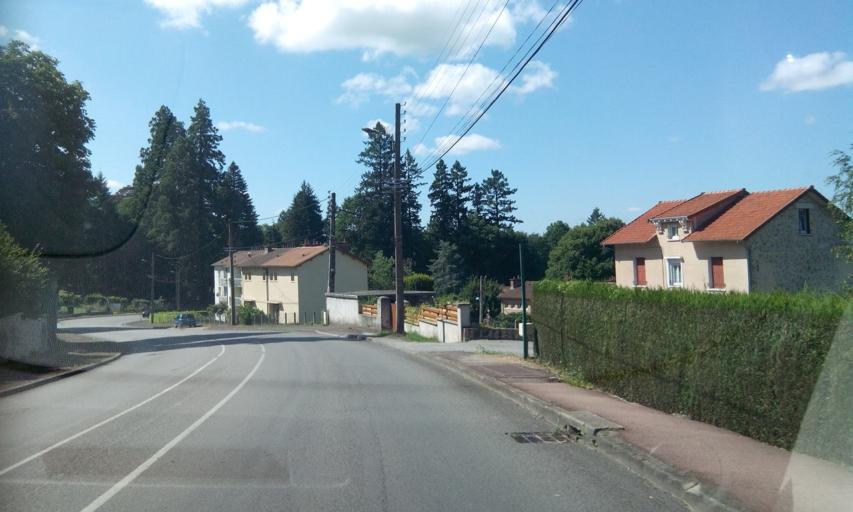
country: FR
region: Limousin
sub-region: Departement de la Haute-Vienne
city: Saint-Leonard-de-Noblat
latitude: 45.8335
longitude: 1.4873
